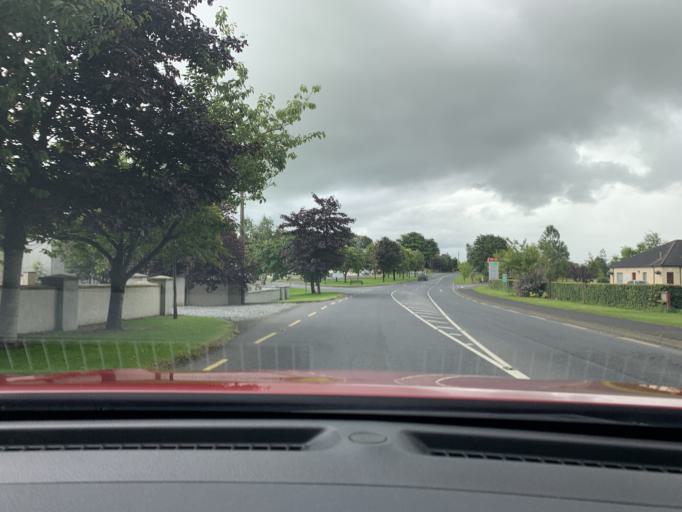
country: IE
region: Ulster
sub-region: County Donegal
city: Raphoe
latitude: 54.8030
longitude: -7.5881
